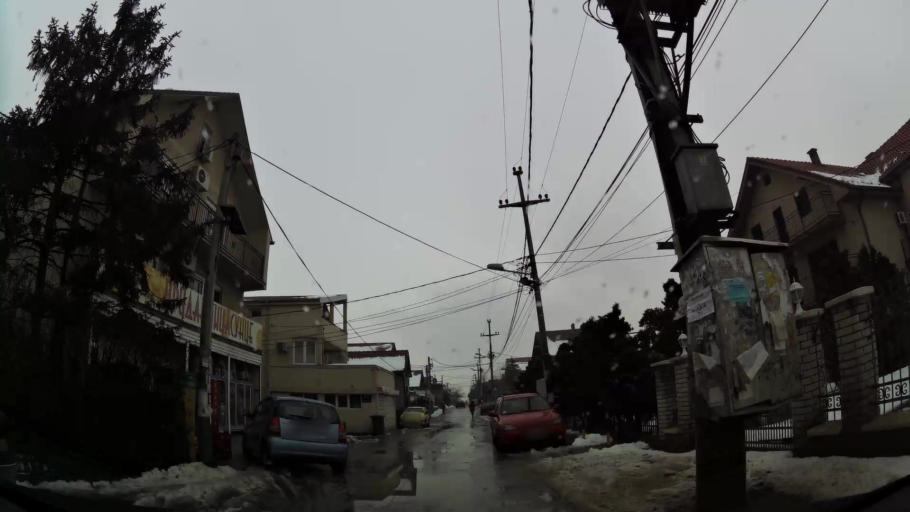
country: RS
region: Central Serbia
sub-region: Belgrade
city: Zemun
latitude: 44.8441
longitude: 20.3665
